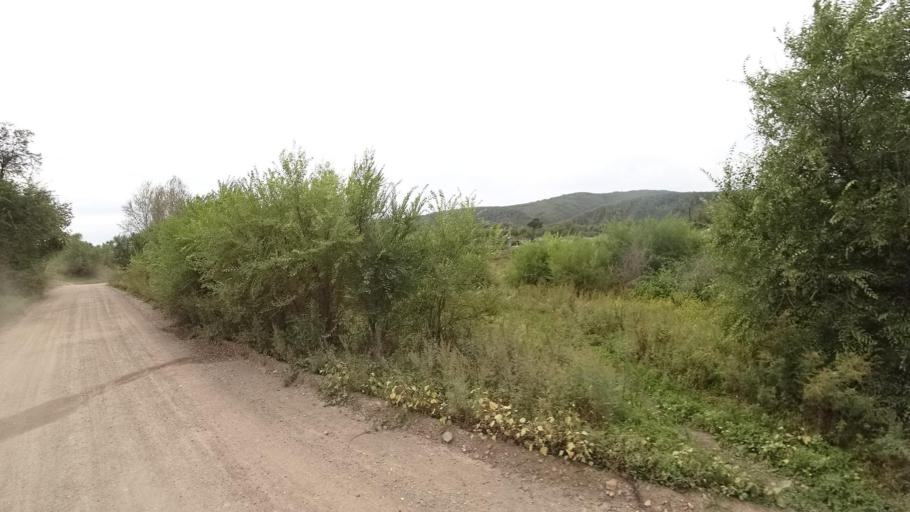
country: RU
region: Jewish Autonomous Oblast
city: Khingansk
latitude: 49.0289
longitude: 131.0574
